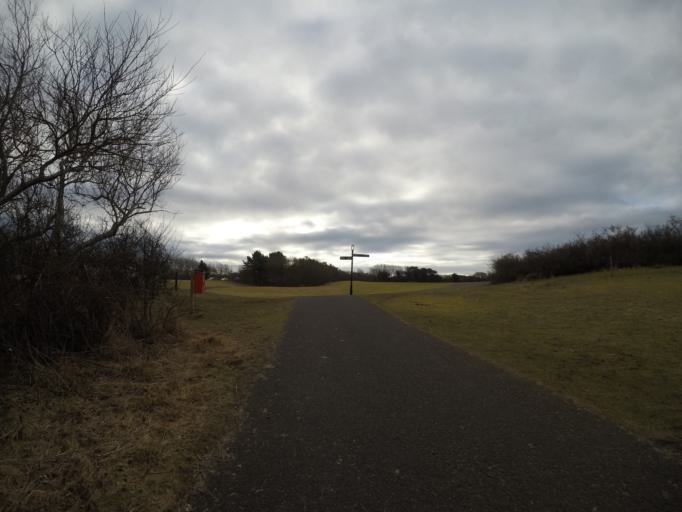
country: GB
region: Scotland
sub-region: North Ayrshire
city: Irvine
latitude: 55.6060
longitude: -4.6821
